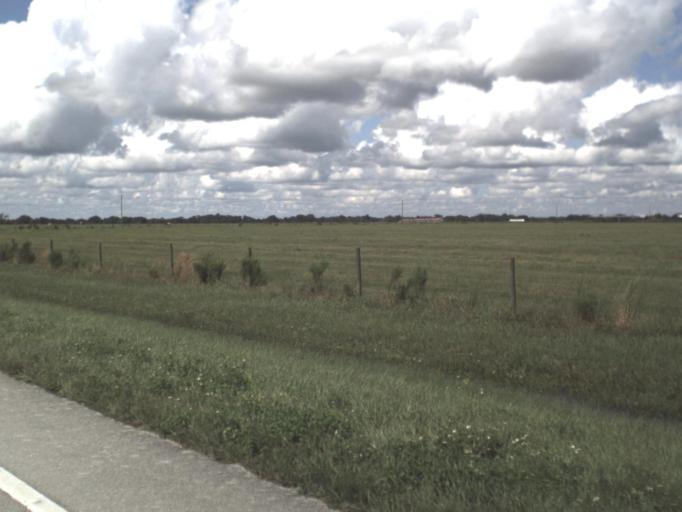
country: US
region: Florida
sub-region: DeSoto County
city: Arcadia
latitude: 27.2432
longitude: -81.9466
